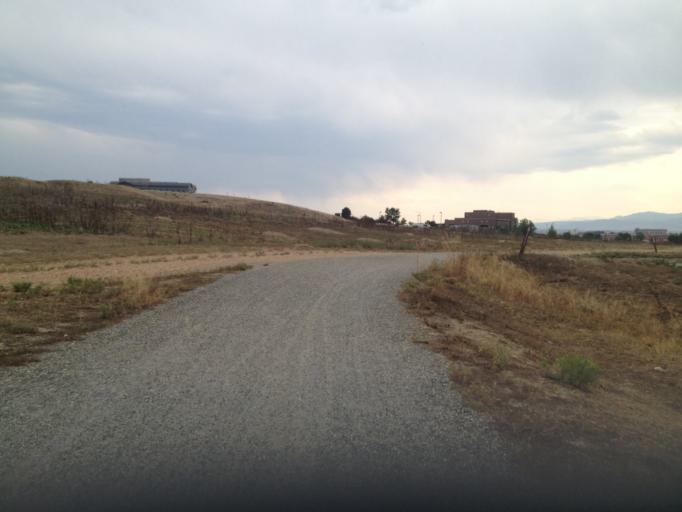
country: US
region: Colorado
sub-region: Boulder County
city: Lafayette
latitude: 39.9849
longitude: -105.0630
